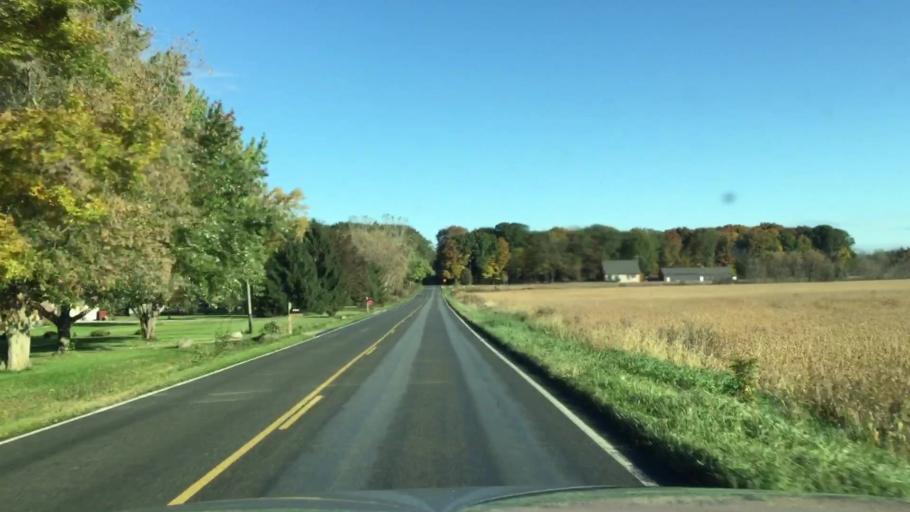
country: US
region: Michigan
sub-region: Shiawassee County
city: Durand
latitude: 42.9274
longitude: -83.9487
